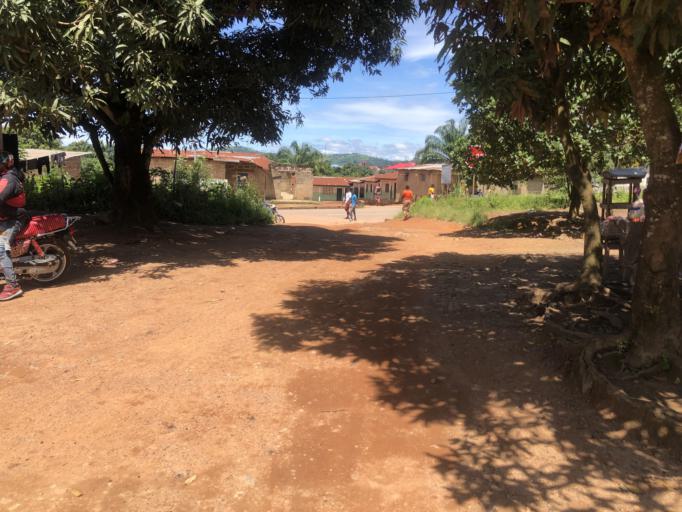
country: SL
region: Eastern Province
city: Koidu
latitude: 8.6418
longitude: -10.9661
